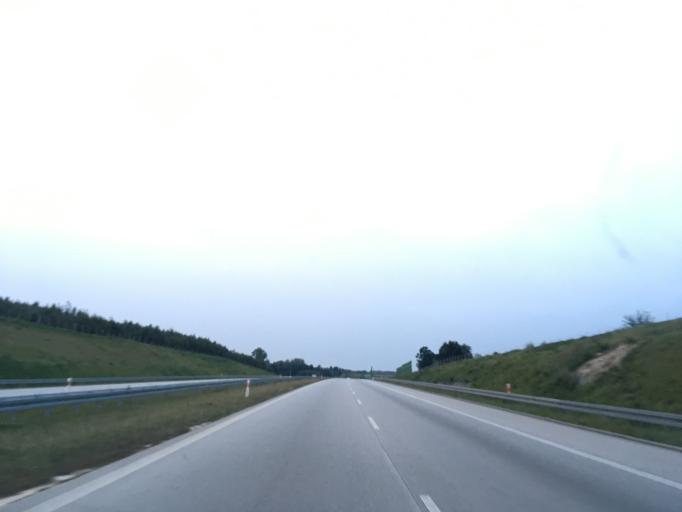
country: PL
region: Lodz Voivodeship
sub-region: Powiat zgierski
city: Strykow
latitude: 51.8305
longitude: 19.6541
